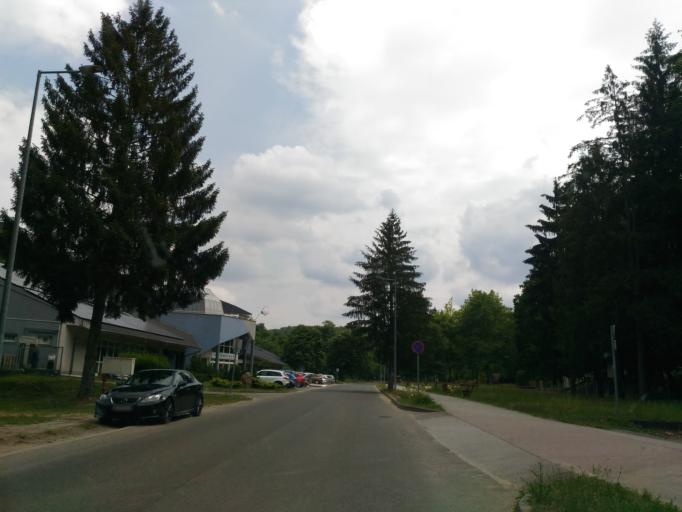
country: HU
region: Baranya
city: Komlo
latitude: 46.1772
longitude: 18.2212
